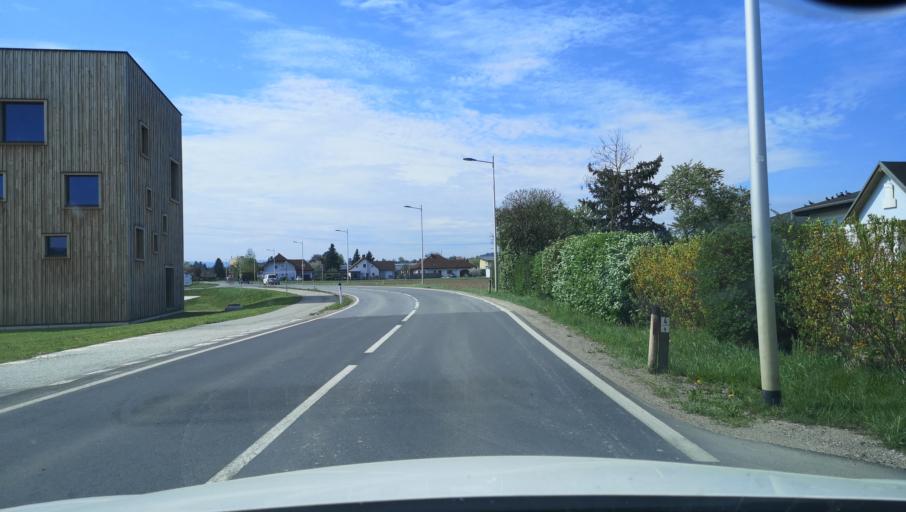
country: AT
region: Lower Austria
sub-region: Politischer Bezirk Melk
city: Petzenkirchen
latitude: 48.1396
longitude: 15.1468
